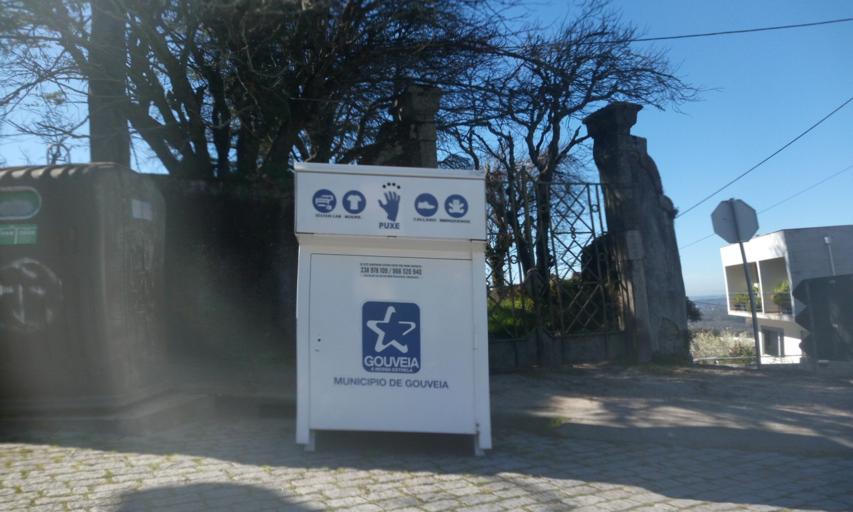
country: PT
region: Guarda
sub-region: Manteigas
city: Manteigas
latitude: 40.4913
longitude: -7.5978
